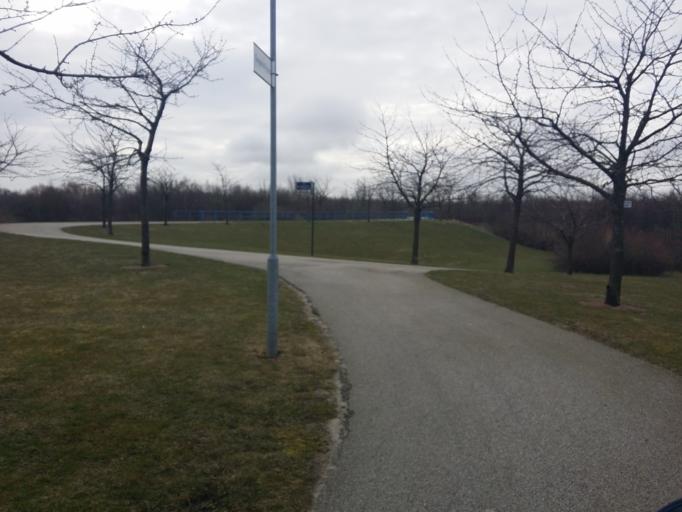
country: SE
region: Skane
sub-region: Burlovs Kommun
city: Arloev
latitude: 55.6091
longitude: 13.0843
